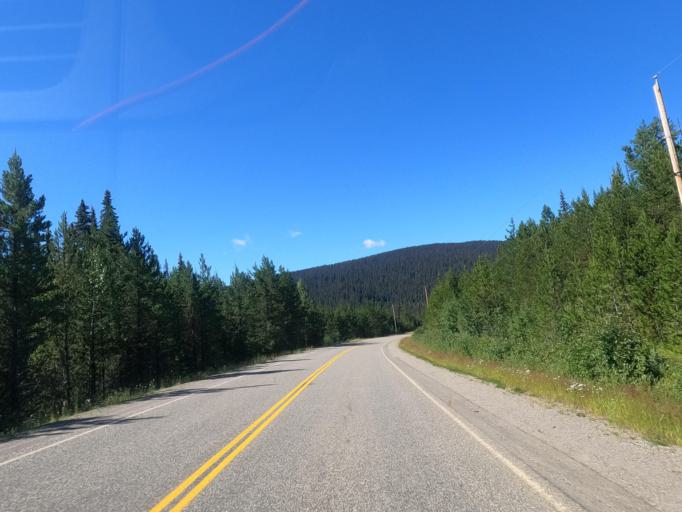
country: CA
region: British Columbia
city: Quesnel
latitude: 53.0448
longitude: -121.7155
